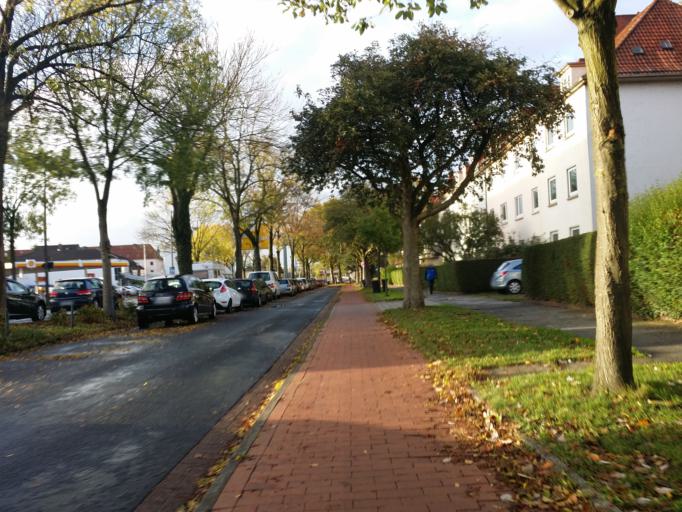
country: DE
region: Bremen
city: Bremen
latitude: 53.0654
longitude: 8.7848
